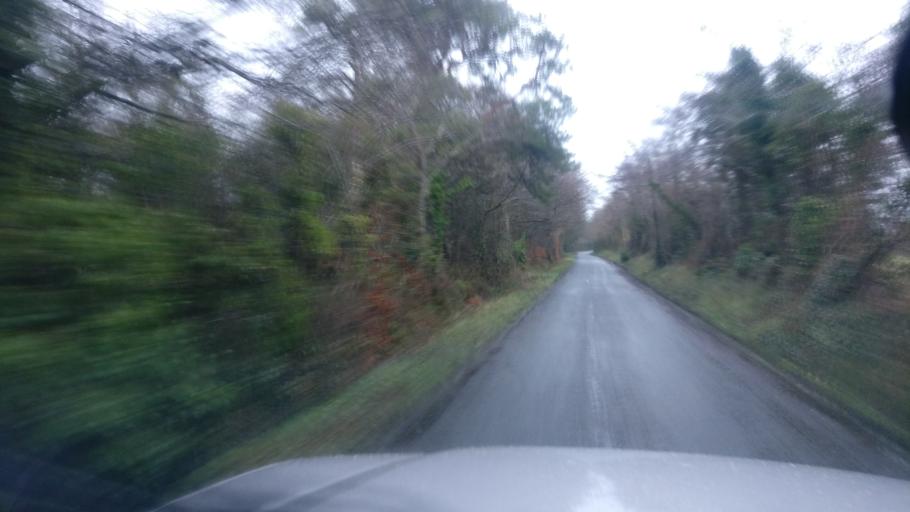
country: IE
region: Connaught
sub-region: County Galway
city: Ballinasloe
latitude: 53.3213
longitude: -8.3804
